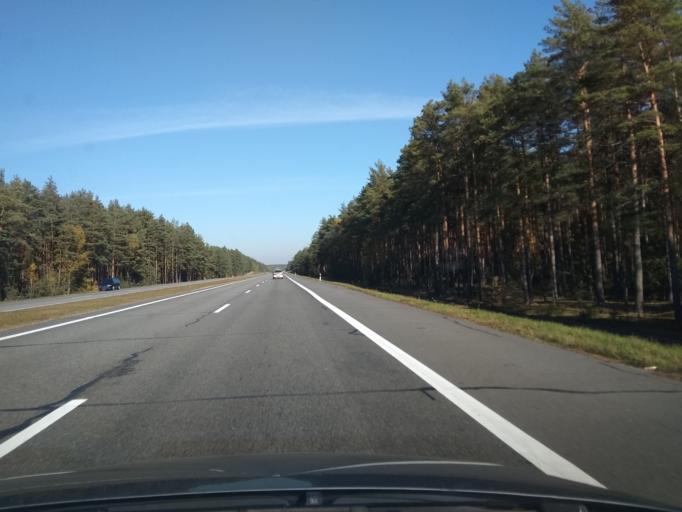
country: BY
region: Brest
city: Baranovichi
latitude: 53.0037
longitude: 25.7695
